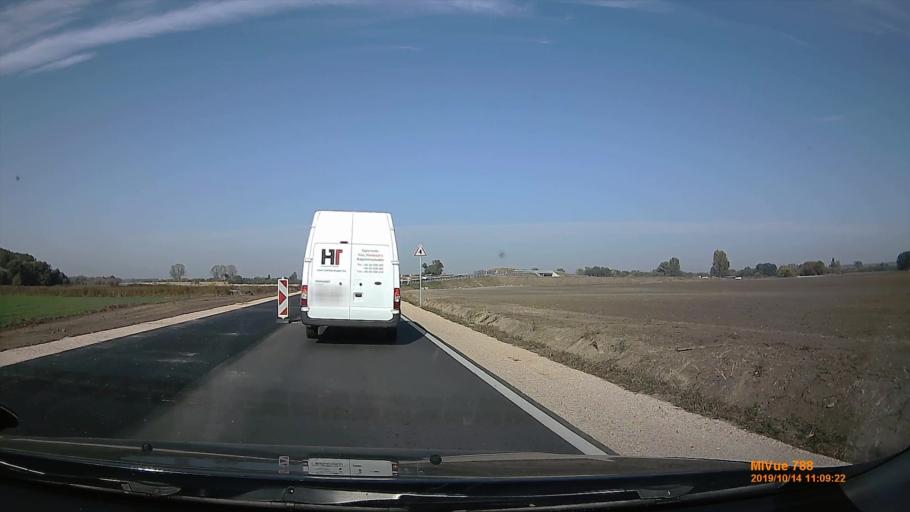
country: HU
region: Pest
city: Peteri
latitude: 47.3679
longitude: 19.4244
